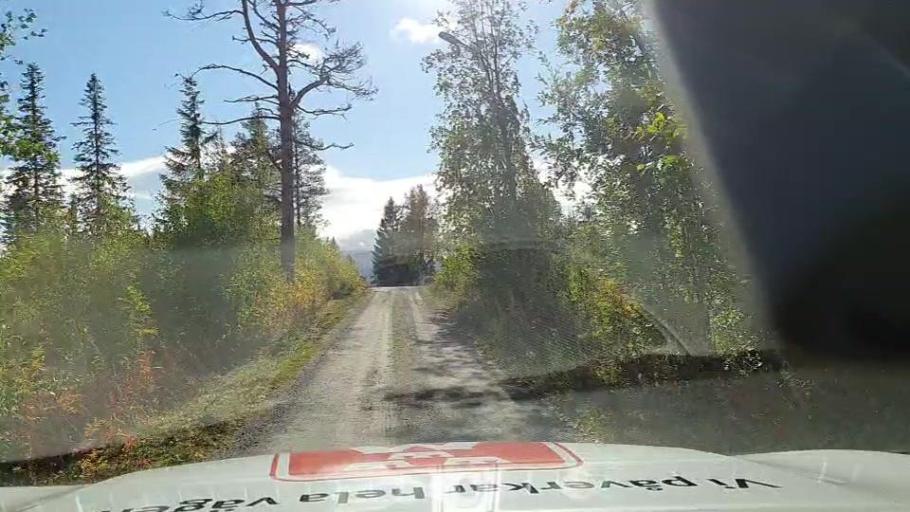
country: SE
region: Jaemtland
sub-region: Are Kommun
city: Jarpen
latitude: 63.2323
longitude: 13.6778
